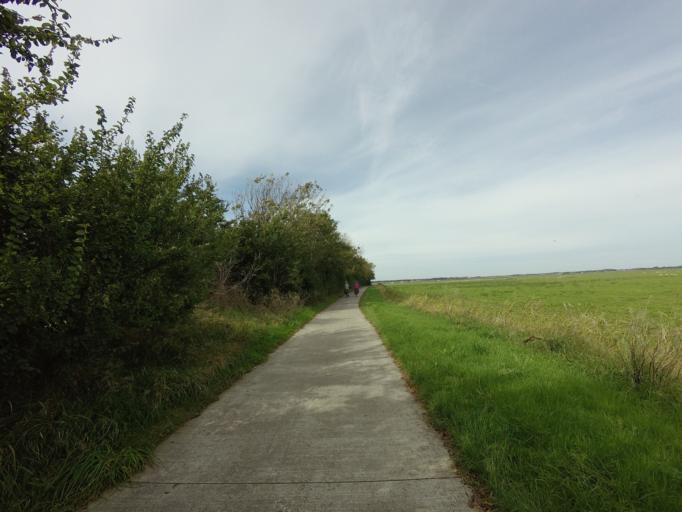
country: NL
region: North Holland
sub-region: Gemeente Texel
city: Den Burg
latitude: 53.0732
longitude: 4.8089
